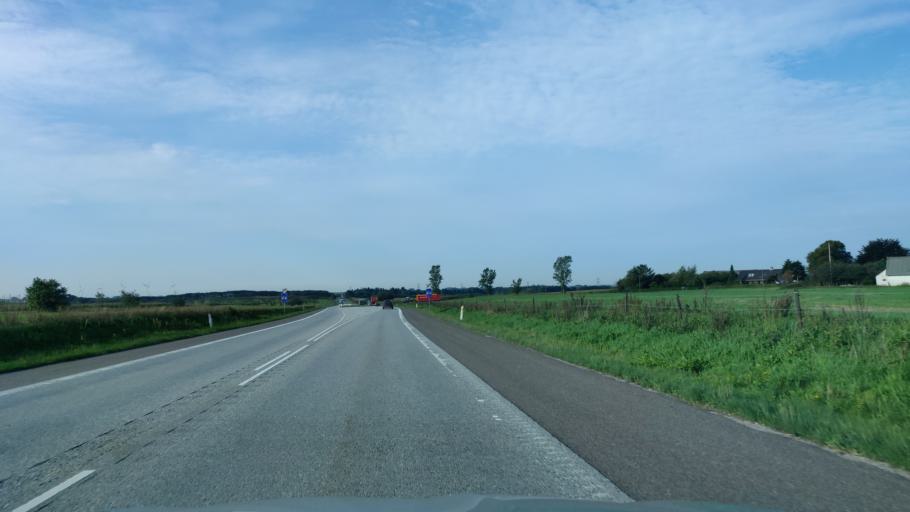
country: DK
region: North Denmark
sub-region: Vesthimmerland Kommune
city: Aars
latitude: 56.8105
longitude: 9.6561
